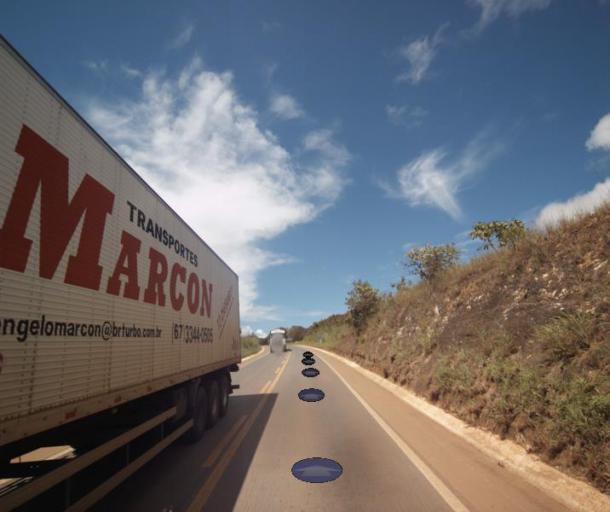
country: BR
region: Goias
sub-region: Padre Bernardo
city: Padre Bernardo
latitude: -15.3543
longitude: -48.2302
